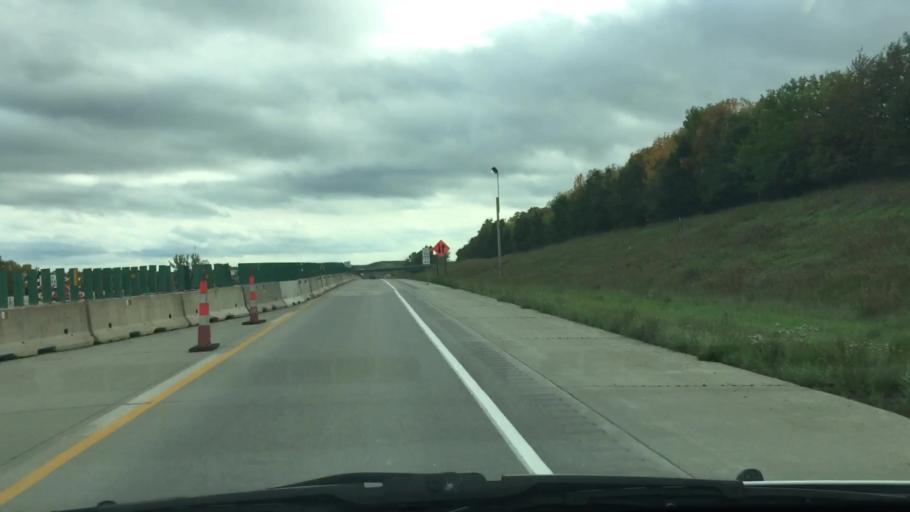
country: US
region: Iowa
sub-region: Decatur County
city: Leon
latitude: 40.7294
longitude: -93.8435
